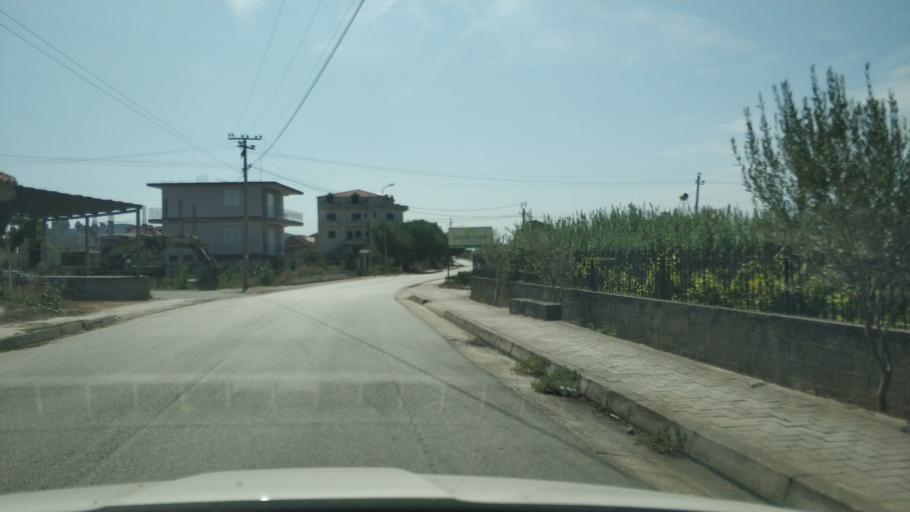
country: AL
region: Fier
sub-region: Rrethi i Lushnjes
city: Divjake
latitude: 40.9782
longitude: 19.5355
